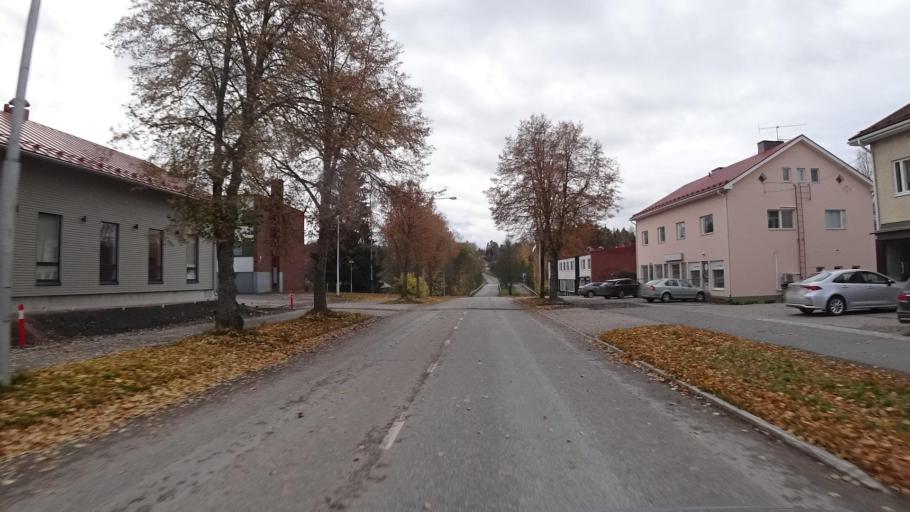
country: FI
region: Central Finland
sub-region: Joutsa
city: Joutsa
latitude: 61.7393
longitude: 26.1121
